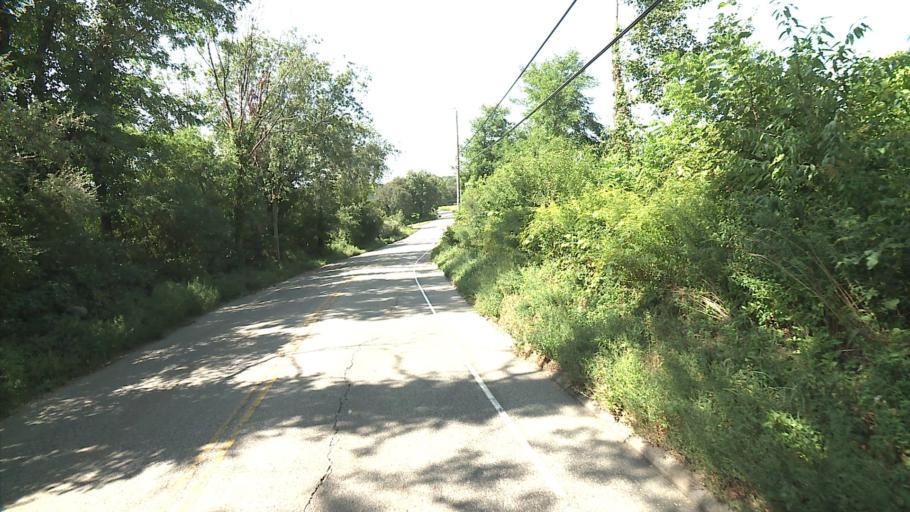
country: US
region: Connecticut
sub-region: Windham County
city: South Windham
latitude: 41.6134
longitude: -72.1857
